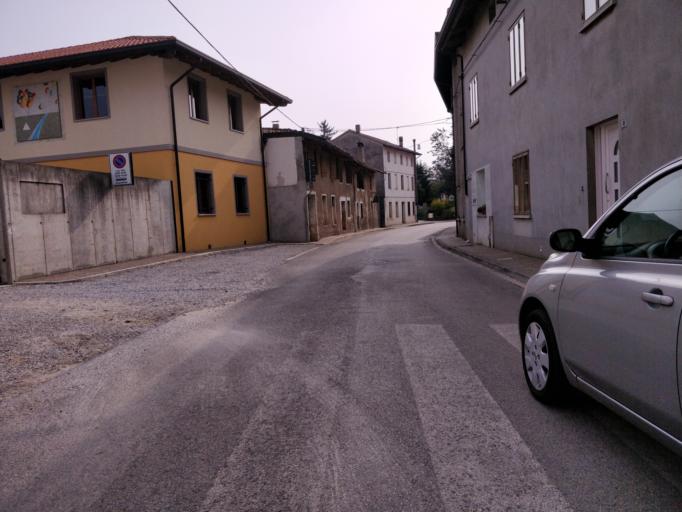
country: IT
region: Friuli Venezia Giulia
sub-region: Provincia di Udine
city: Bertiolo
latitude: 45.9412
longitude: 13.0526
